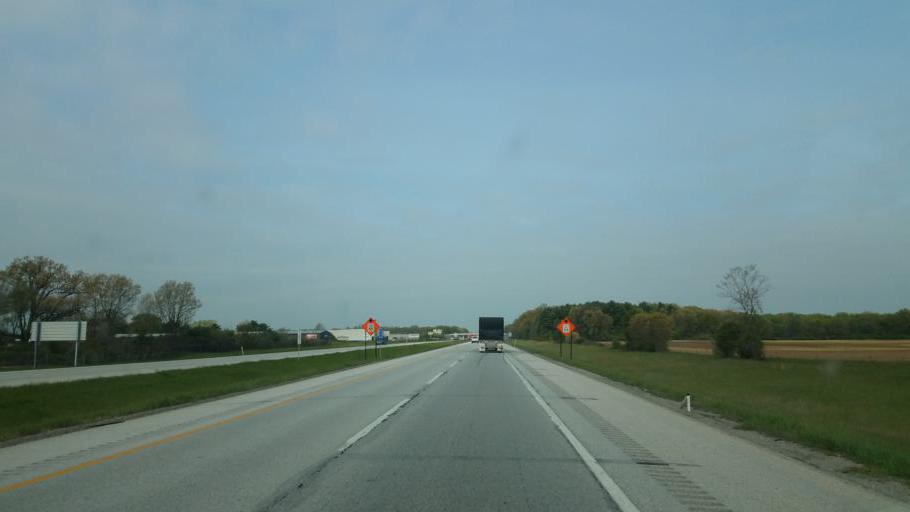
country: US
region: Indiana
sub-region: Elkhart County
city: Simonton Lake
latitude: 41.7294
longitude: -85.9160
